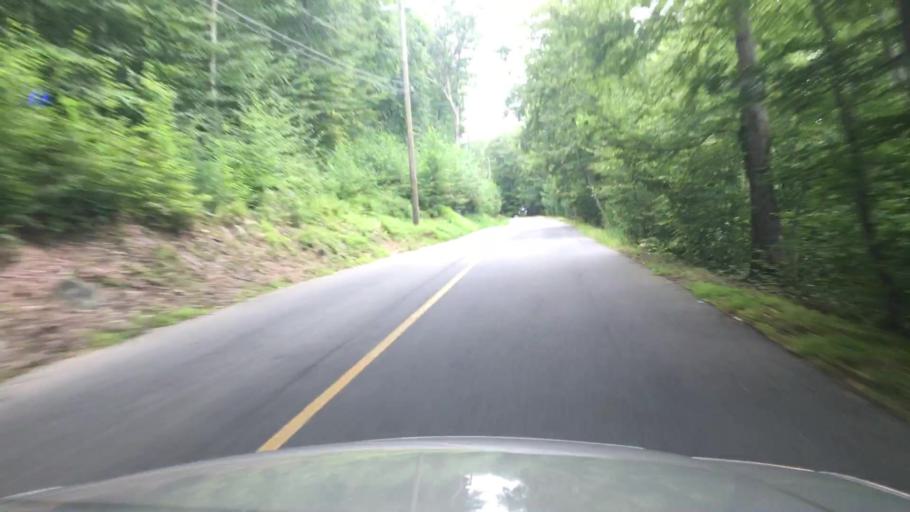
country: US
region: Connecticut
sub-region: Middlesex County
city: Deep River Center
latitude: 41.3868
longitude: -72.4092
